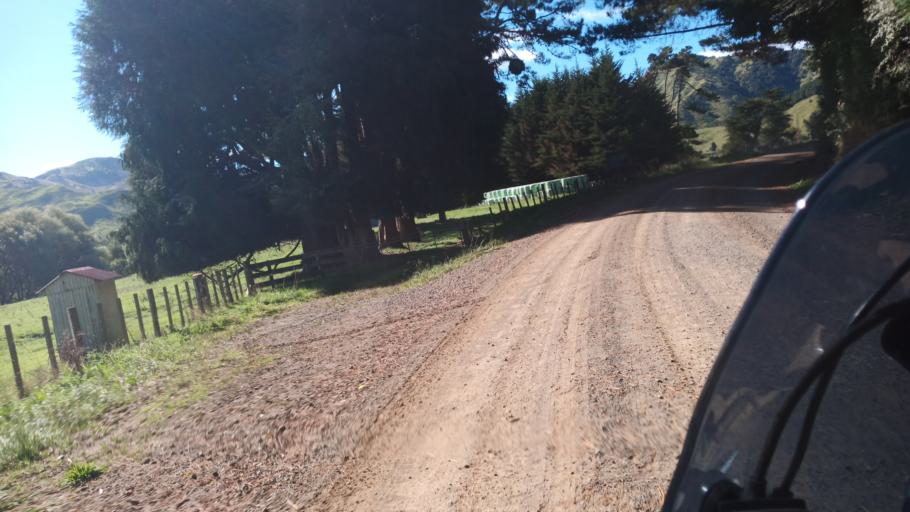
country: NZ
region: Bay of Plenty
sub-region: Opotiki District
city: Opotiki
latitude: -38.2566
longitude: 177.5694
